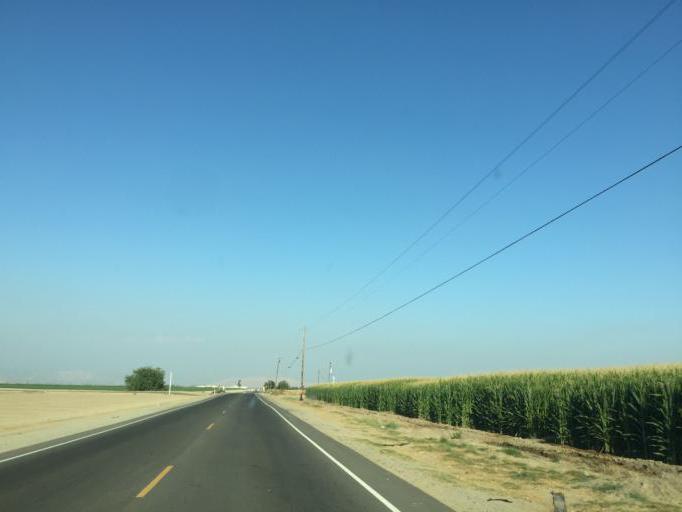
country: US
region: California
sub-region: Tulare County
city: Dinuba
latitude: 36.4582
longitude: -119.3519
